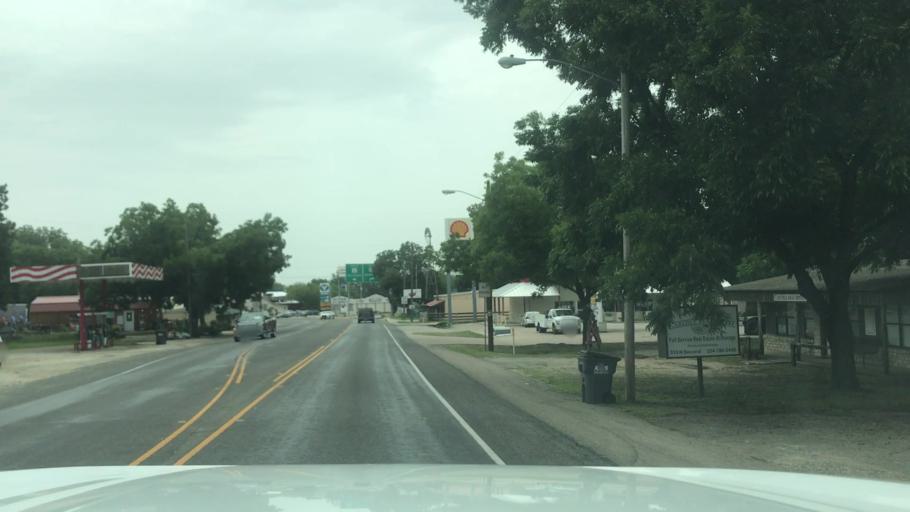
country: US
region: Texas
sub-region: Hamilton County
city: Hico
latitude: 31.9846
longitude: -98.0353
